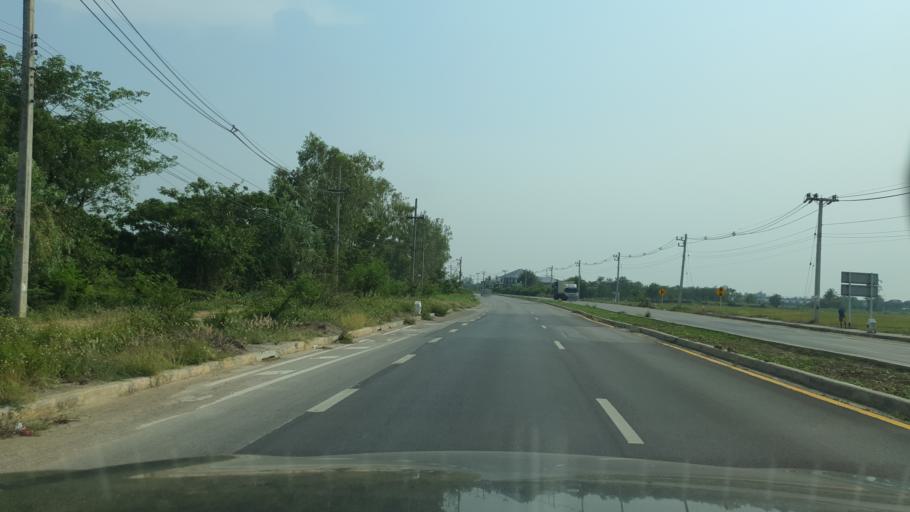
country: TH
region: Lamphun
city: Lamphun
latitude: 18.5926
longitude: 98.9992
